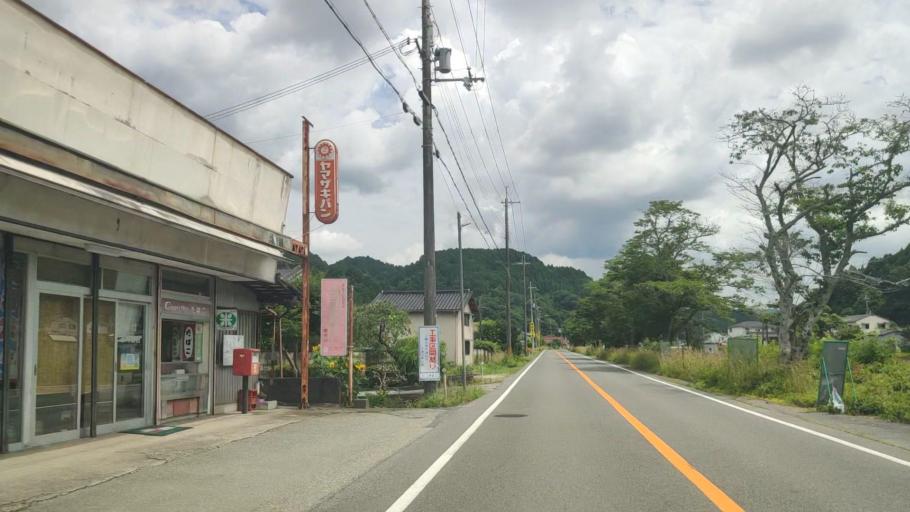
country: JP
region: Hyogo
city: Yamazakicho-nakabirose
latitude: 34.9784
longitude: 134.4432
